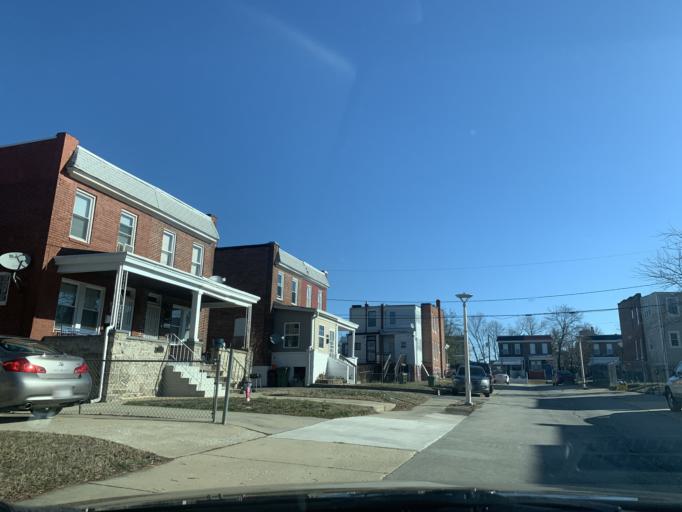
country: US
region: Maryland
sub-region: Baltimore County
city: Lochearn
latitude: 39.3323
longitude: -76.6880
